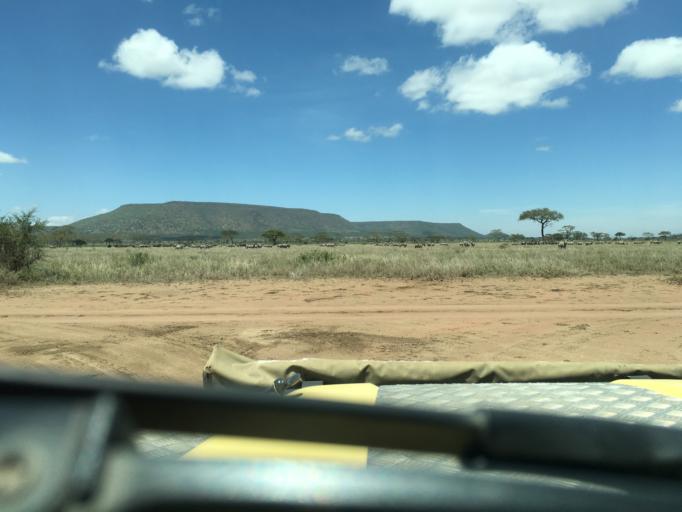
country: TZ
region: Simiyu
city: Kisesa
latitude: -2.6737
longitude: 34.7821
